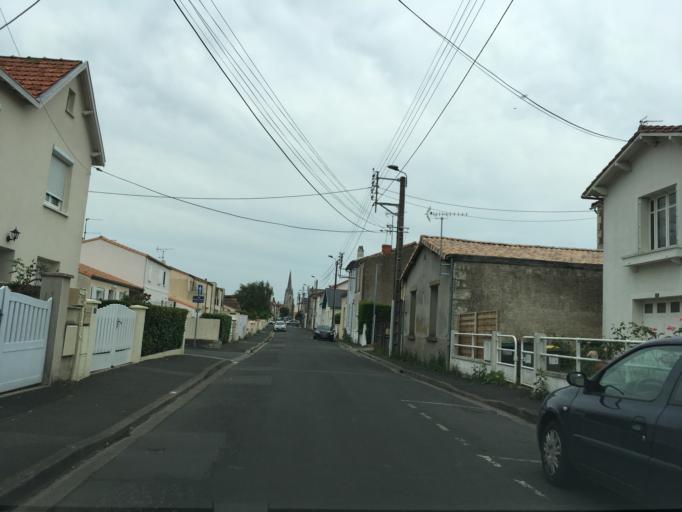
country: FR
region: Poitou-Charentes
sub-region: Departement des Deux-Sevres
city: Niort
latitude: 46.3148
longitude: -0.4694
